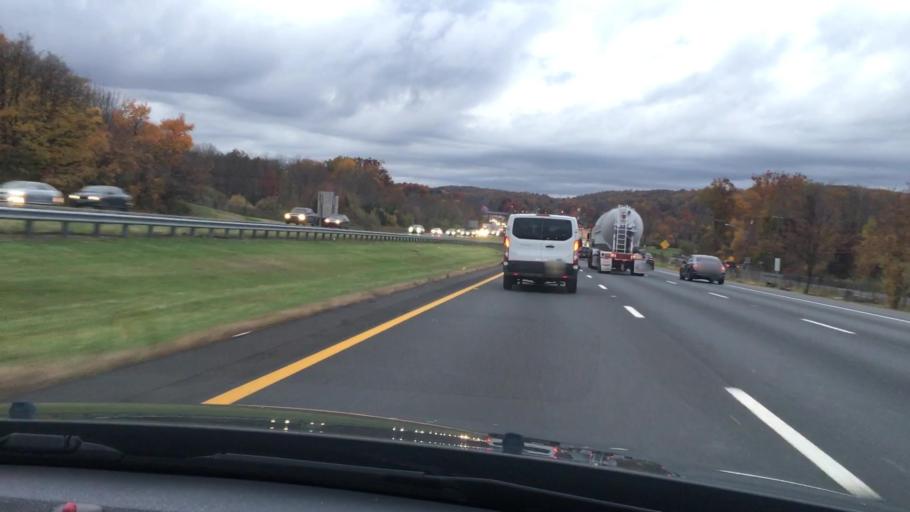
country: US
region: New Jersey
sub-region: Hunterdon County
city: Glen Gardner
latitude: 40.6395
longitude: -74.9847
